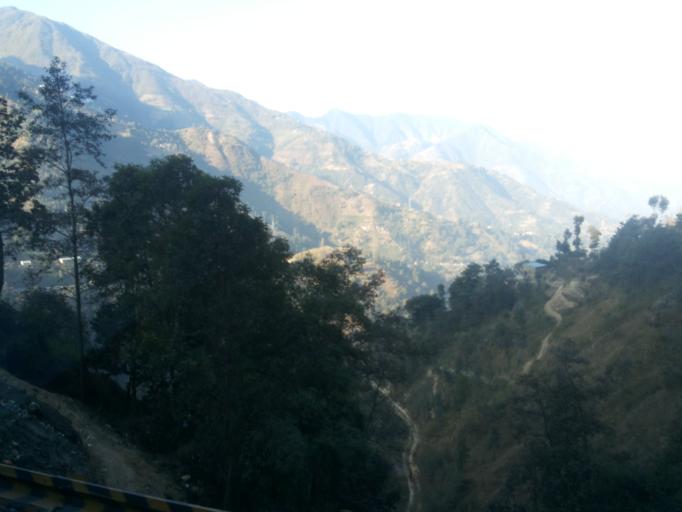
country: NP
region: Central Region
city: Kirtipur
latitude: 27.7126
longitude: 85.2005
